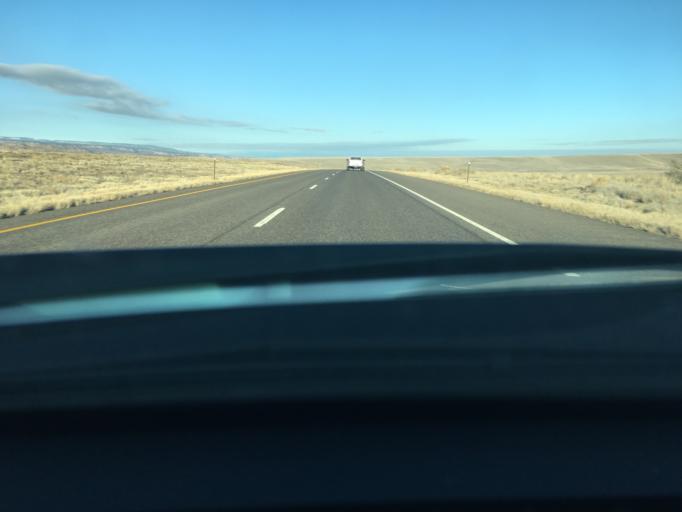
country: US
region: Colorado
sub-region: Delta County
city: Delta
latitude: 38.8006
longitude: -108.2690
